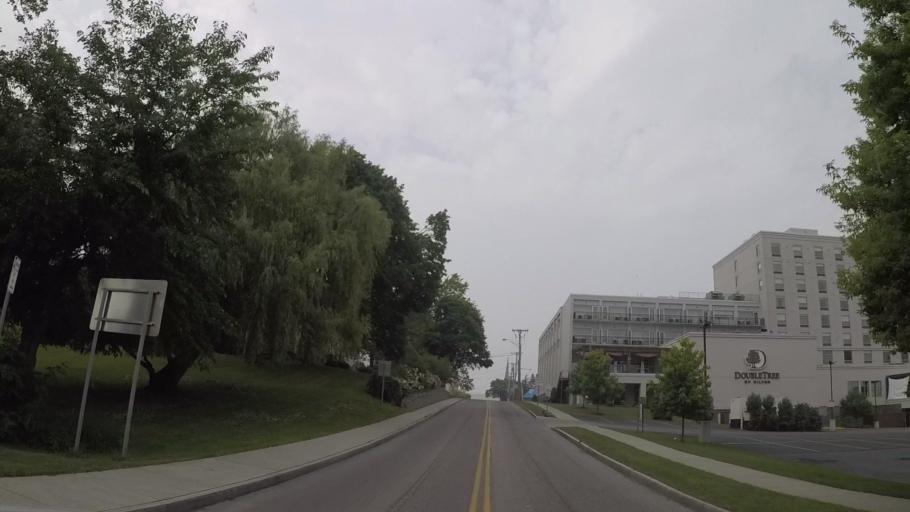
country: US
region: New York
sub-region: Niagara County
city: Niagara Falls
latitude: 43.0812
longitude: -79.0572
